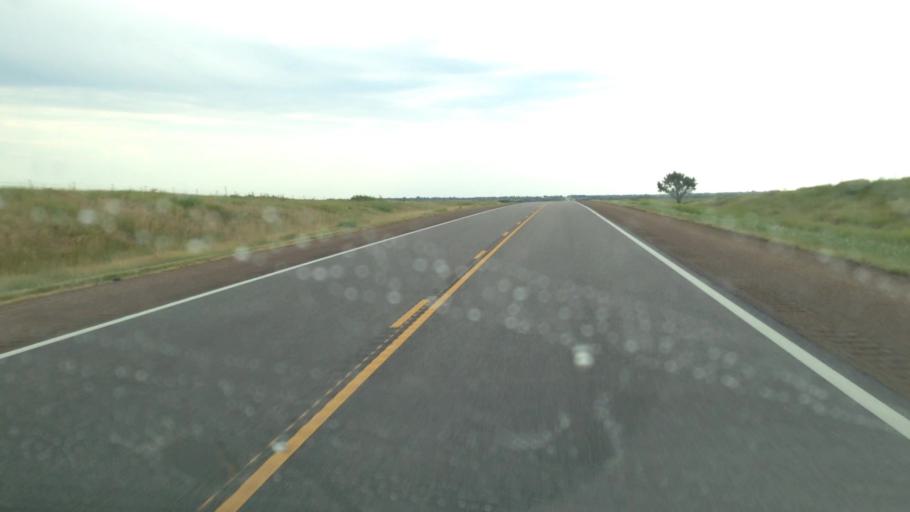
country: US
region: Kansas
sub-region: Coffey County
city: Burlington
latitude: 38.0478
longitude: -95.7391
